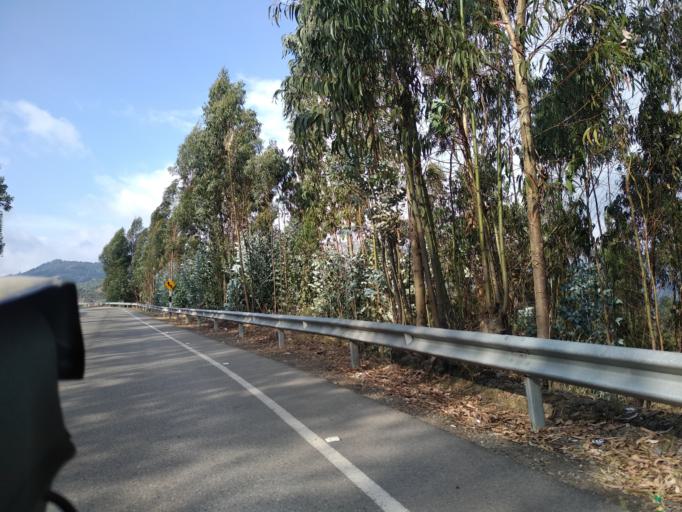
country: PE
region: La Libertad
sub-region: Provincia de Otuzco
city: Agallpampa
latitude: -7.9940
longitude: -78.5296
